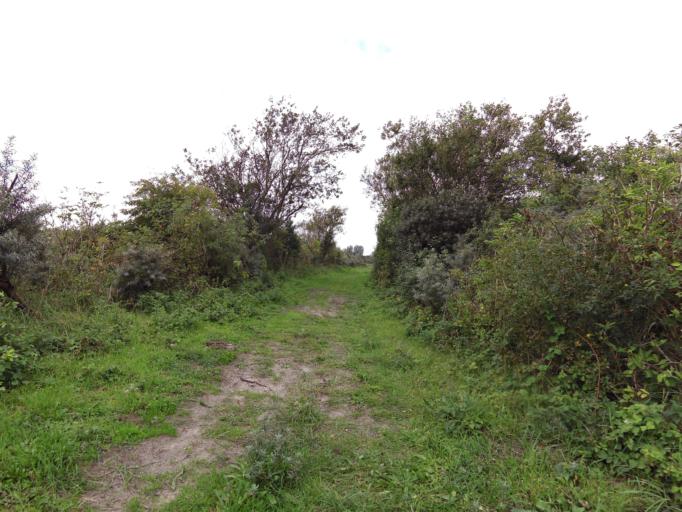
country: NL
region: South Holland
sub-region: Gemeente Goeree-Overflakkee
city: Dirksland
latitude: 51.7681
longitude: 4.0339
